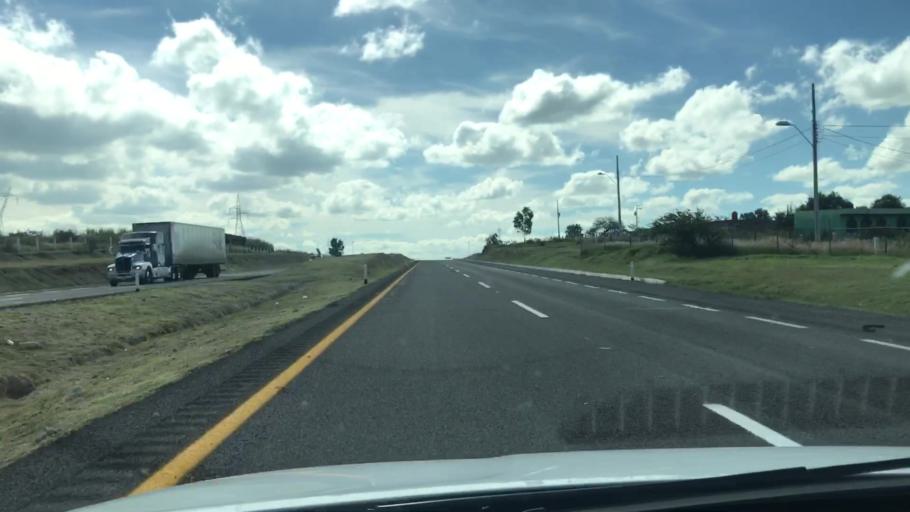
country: MX
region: Guanajuato
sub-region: Silao de la Victoria
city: El Refugio de los Sauces
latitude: 20.9988
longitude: -101.5623
